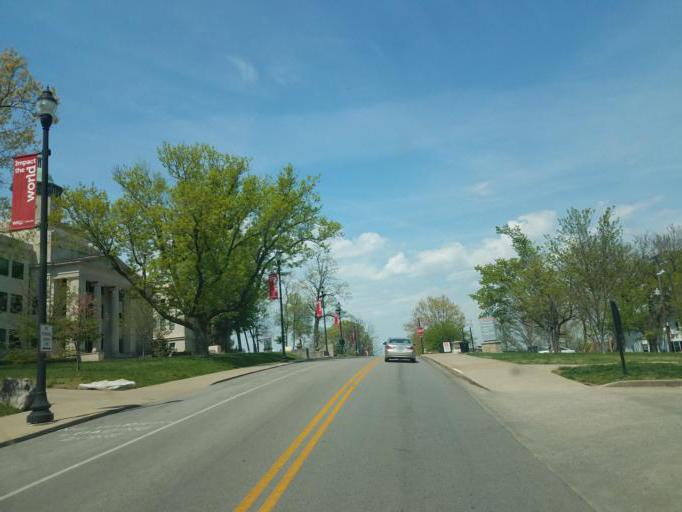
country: US
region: Kentucky
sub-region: Warren County
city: Bowling Green
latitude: 36.9873
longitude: -86.4502
